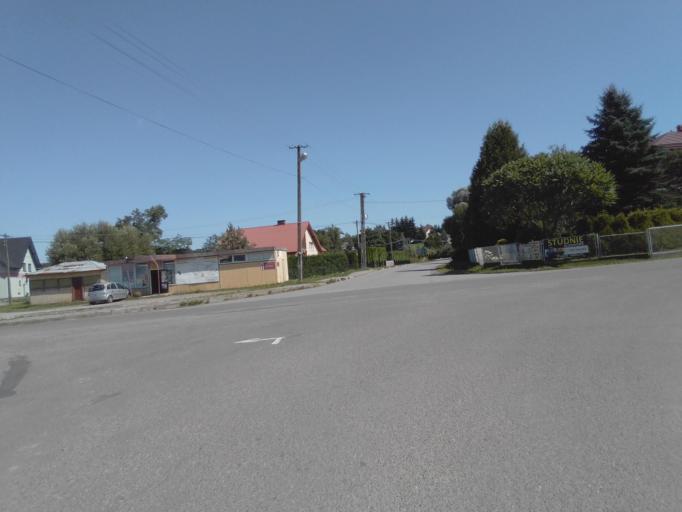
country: PL
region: Subcarpathian Voivodeship
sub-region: Powiat krosnienski
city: Chorkowka
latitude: 49.6655
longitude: 21.6109
